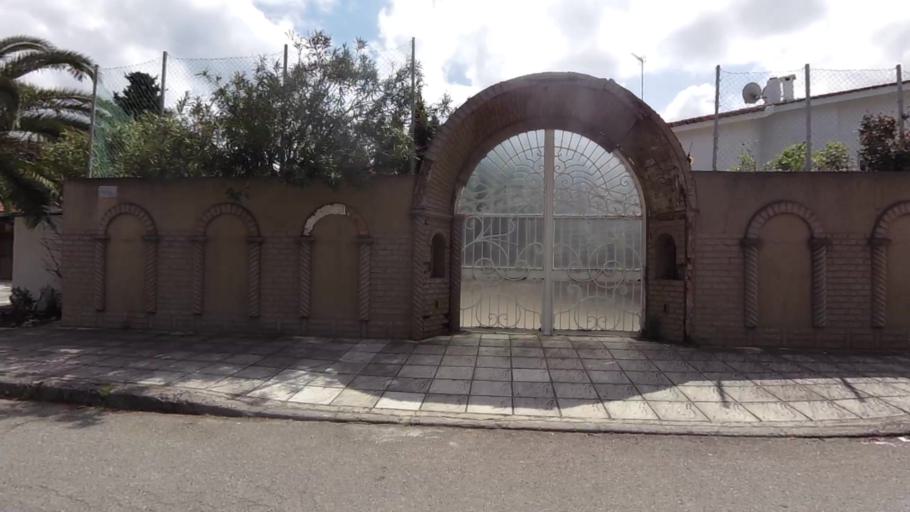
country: MA
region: Tanger-Tetouan
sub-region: Tanger-Assilah
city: Tangier
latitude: 35.7746
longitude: -5.7729
